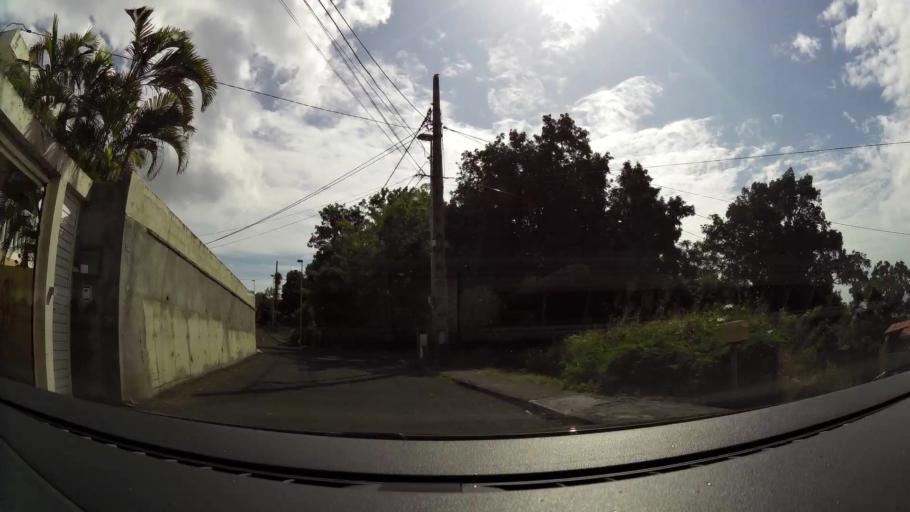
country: GP
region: Guadeloupe
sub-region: Guadeloupe
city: Basse-Terre
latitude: 16.0046
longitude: -61.7345
